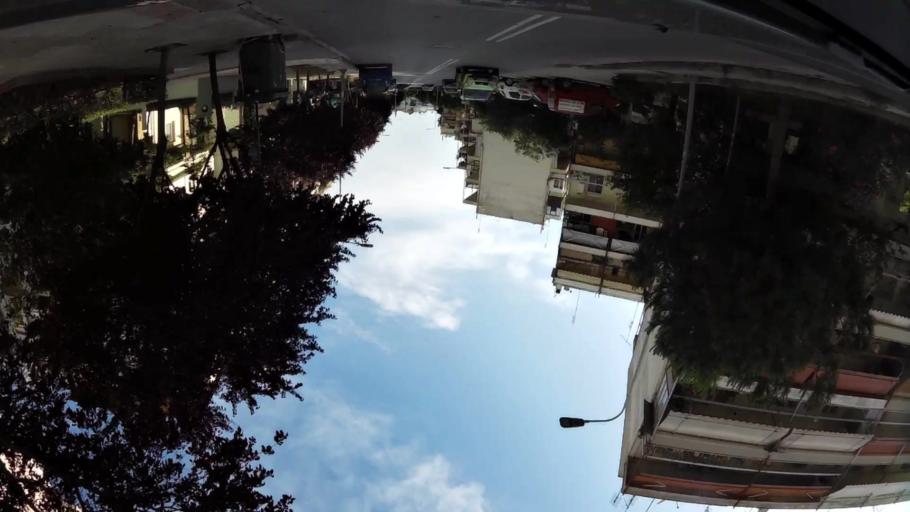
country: GR
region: Central Macedonia
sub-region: Nomos Thessalonikis
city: Kalamaria
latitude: 40.5727
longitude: 22.9636
